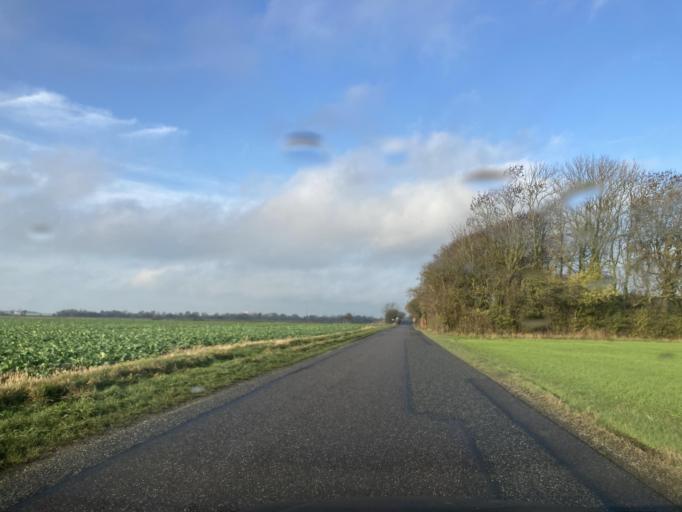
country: DK
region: Zealand
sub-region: Lolland Kommune
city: Rodby
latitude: 54.6834
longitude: 11.4072
